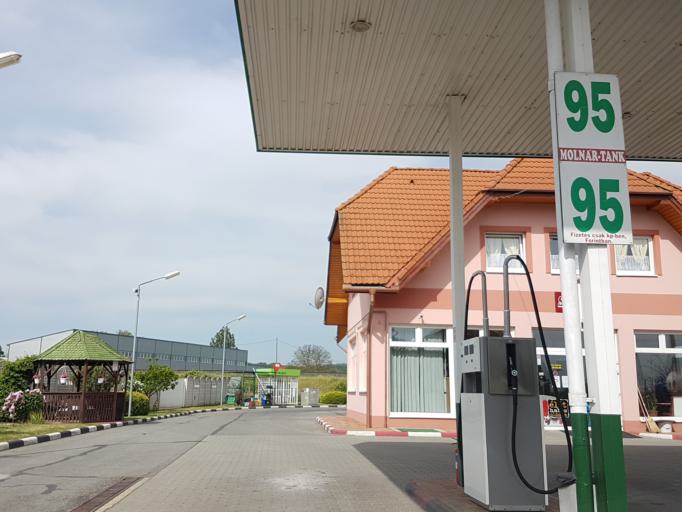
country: HU
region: Zala
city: Zalaegerszeg
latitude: 46.8567
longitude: 16.7900
